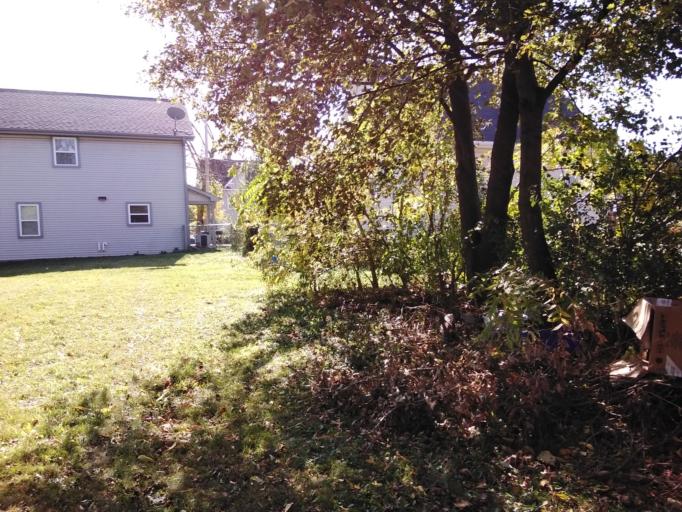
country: US
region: Wisconsin
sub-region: Milwaukee County
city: Milwaukee
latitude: 43.0695
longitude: -87.9371
